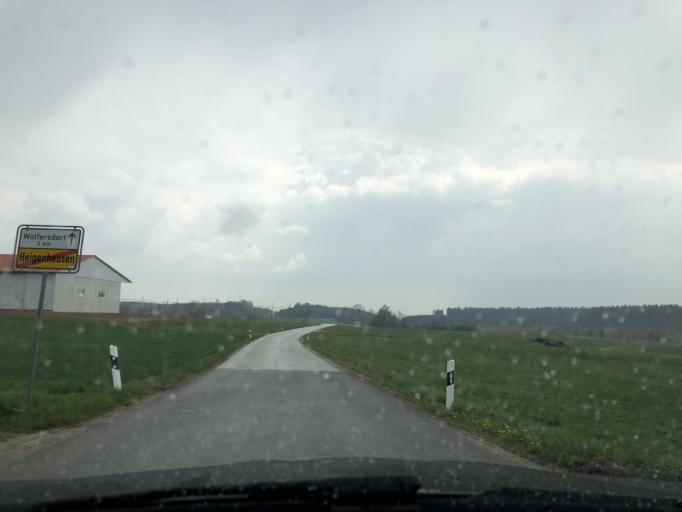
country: DE
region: Bavaria
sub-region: Upper Bavaria
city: Wolfersdorf
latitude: 48.5033
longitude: 11.6790
